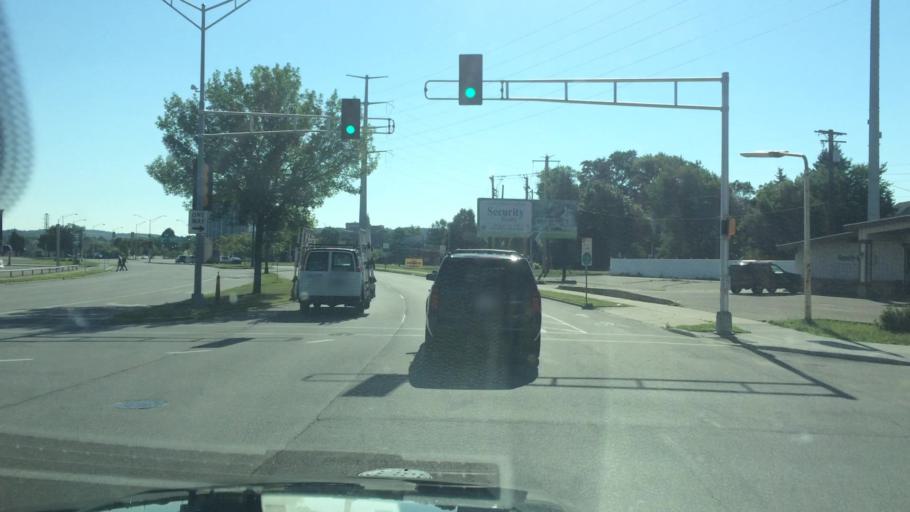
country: US
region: Wisconsin
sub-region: Marathon County
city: Wausau
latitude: 44.9592
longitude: -89.6395
